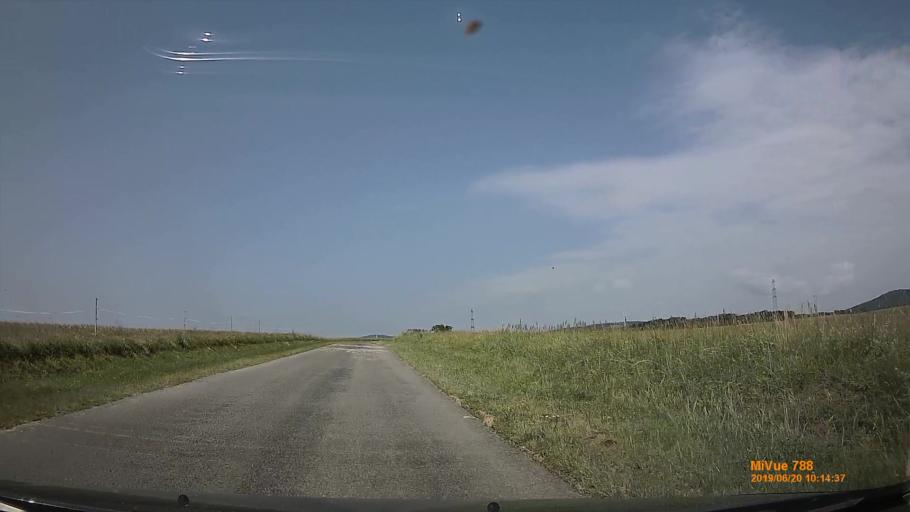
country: HU
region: Baranya
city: Mecseknadasd
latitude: 46.1885
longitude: 18.4720
